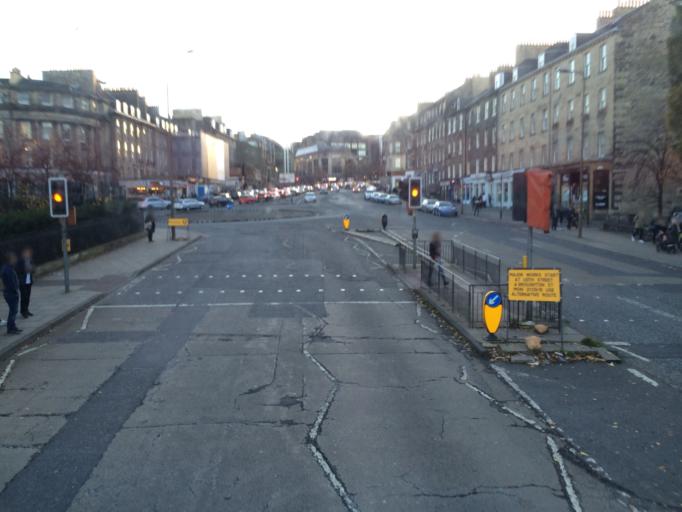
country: GB
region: Scotland
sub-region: Edinburgh
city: Edinburgh
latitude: 55.9586
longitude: -3.1840
